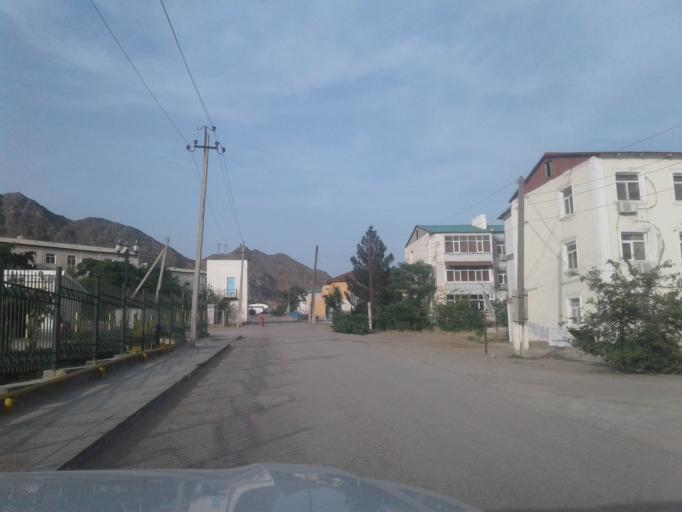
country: TM
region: Balkan
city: Turkmenbasy
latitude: 40.0013
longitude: 52.9730
